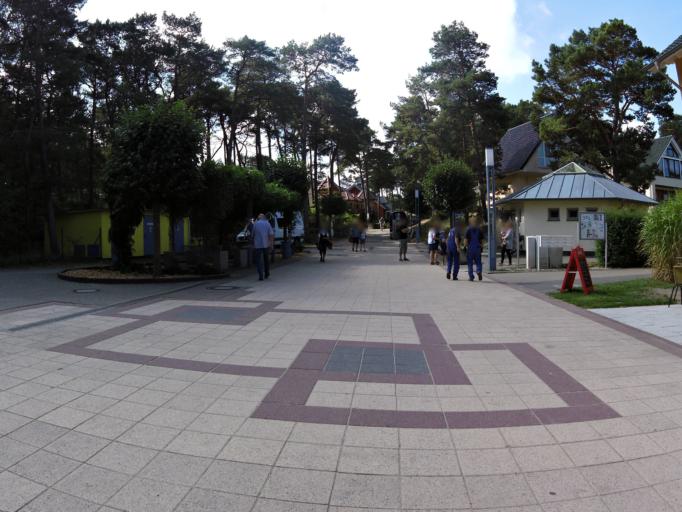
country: DE
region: Mecklenburg-Vorpommern
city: Ostseebad Zinnowitz
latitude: 54.0954
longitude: 13.8788
